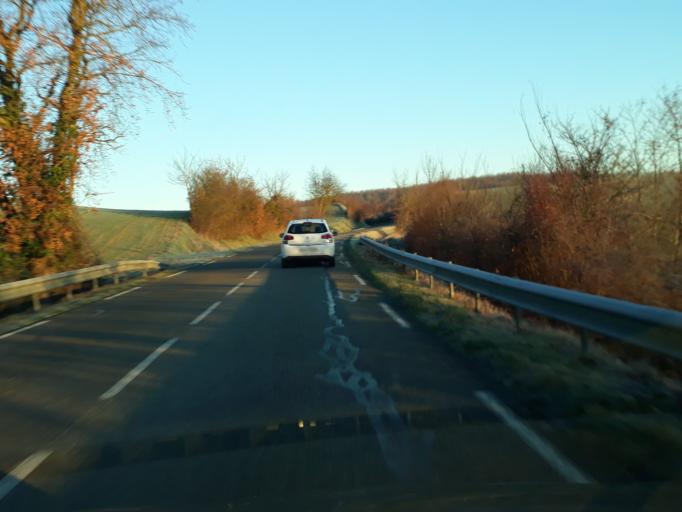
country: FR
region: Midi-Pyrenees
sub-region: Departement du Gers
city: Pavie
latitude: 43.6276
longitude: 0.6344
